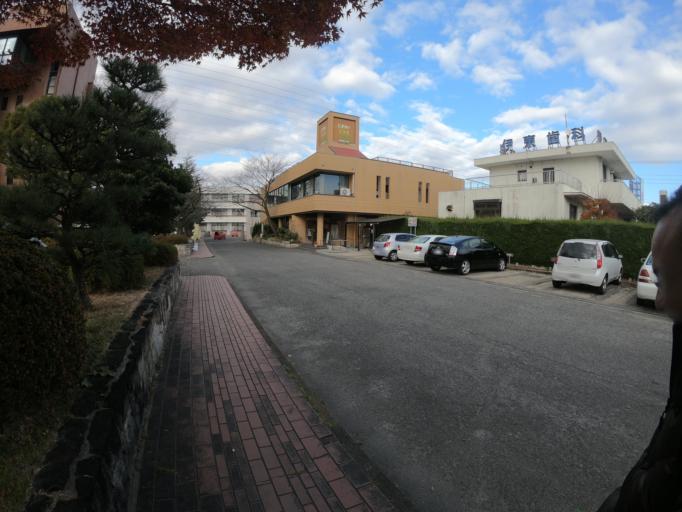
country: JP
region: Aichi
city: Seto
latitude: 35.1317
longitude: 137.0400
